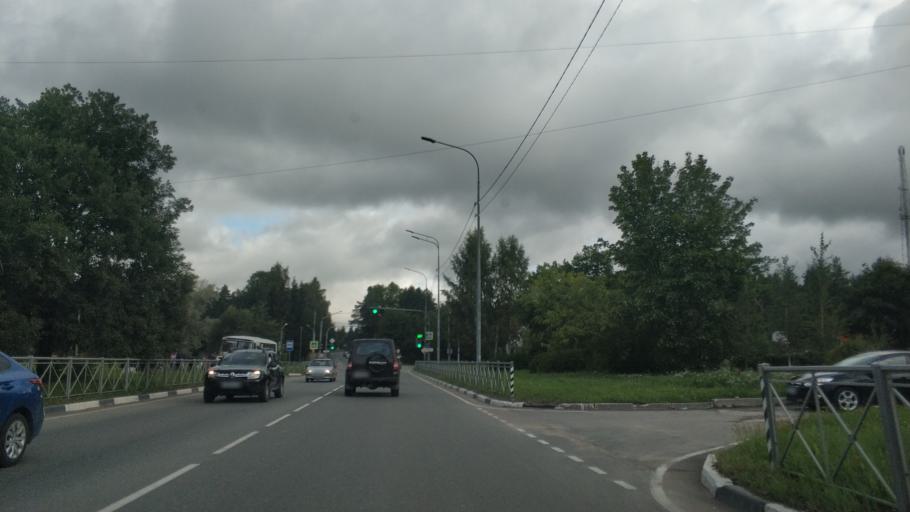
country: RU
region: Republic of Karelia
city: Sortavala
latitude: 61.7112
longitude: 30.6991
